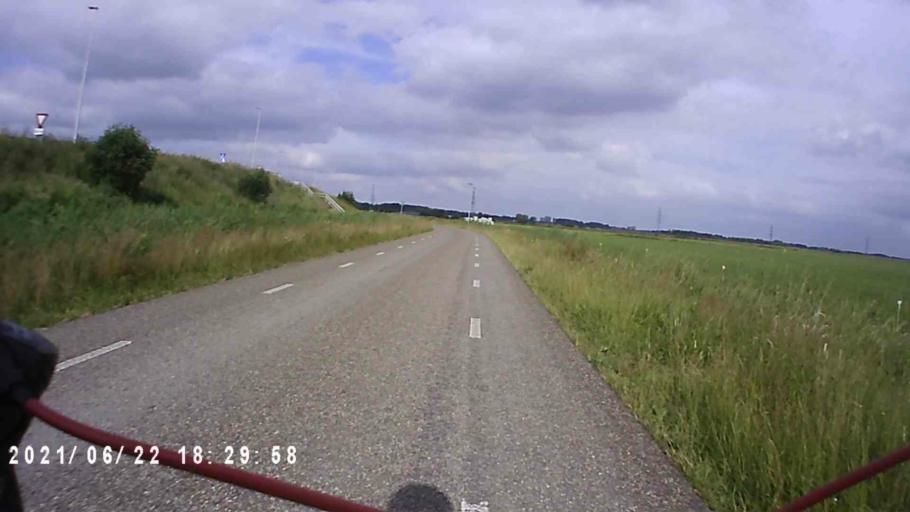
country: NL
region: Groningen
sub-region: Gemeente Zuidhorn
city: Aduard
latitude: 53.2016
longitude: 6.4725
